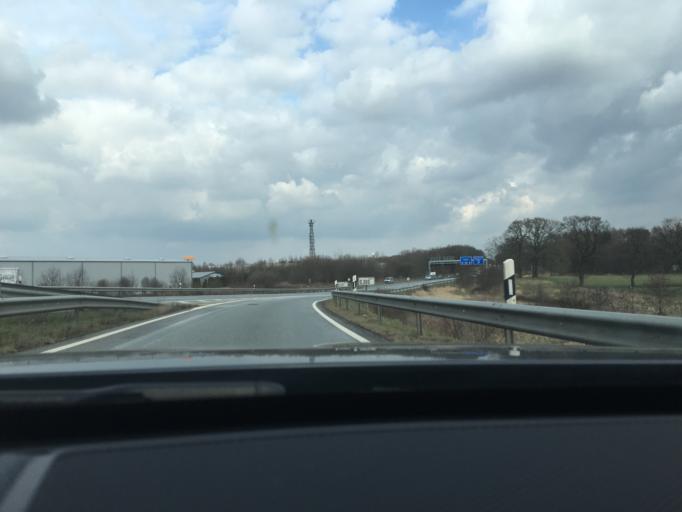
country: DE
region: Lower Saxony
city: Delmenhorst
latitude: 53.0327
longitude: 8.6729
